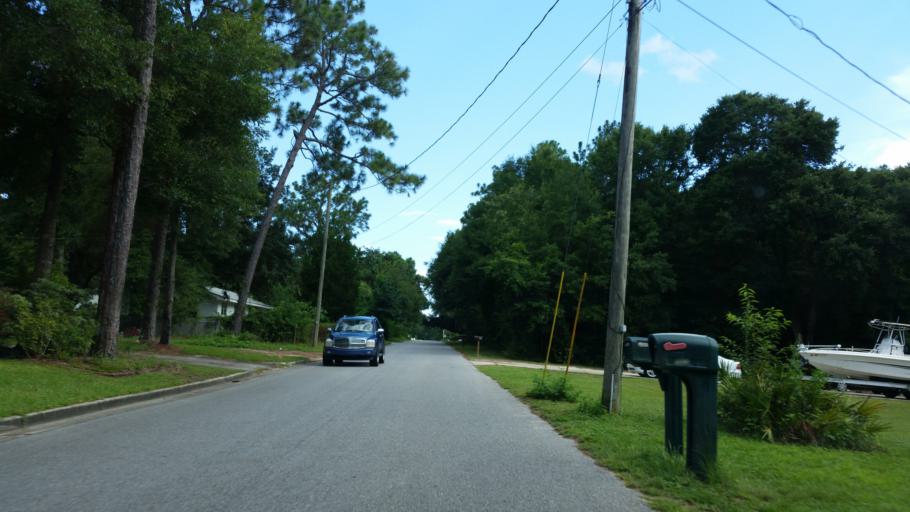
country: US
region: Florida
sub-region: Escambia County
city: Ferry Pass
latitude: 30.5341
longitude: -87.2162
